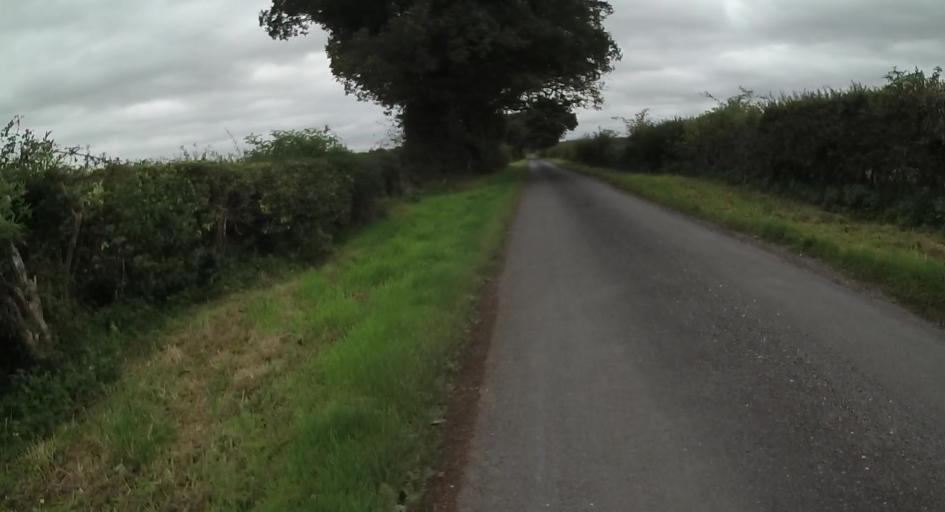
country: GB
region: England
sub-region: Hampshire
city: Four Marks
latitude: 51.1569
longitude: -1.1172
